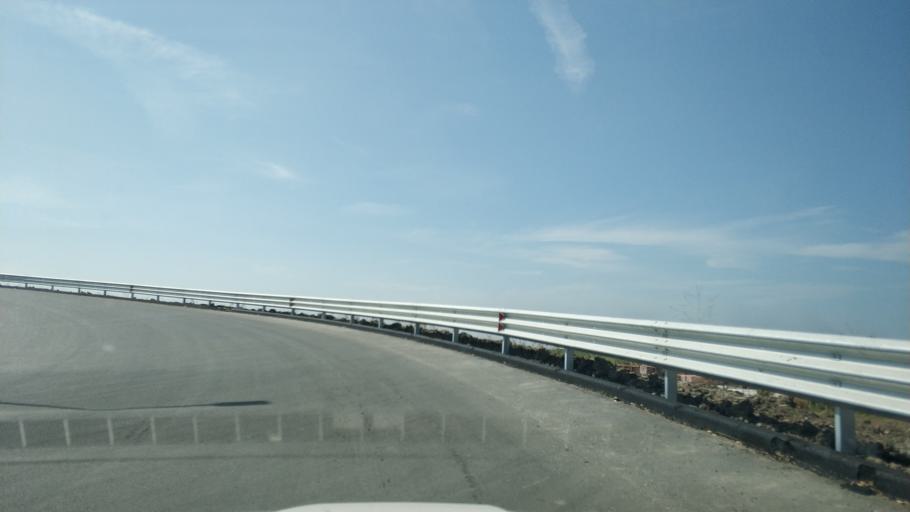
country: AL
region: Fier
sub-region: Rrethi i Fierit
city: Mbrostar-Ure
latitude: 40.7488
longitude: 19.5579
